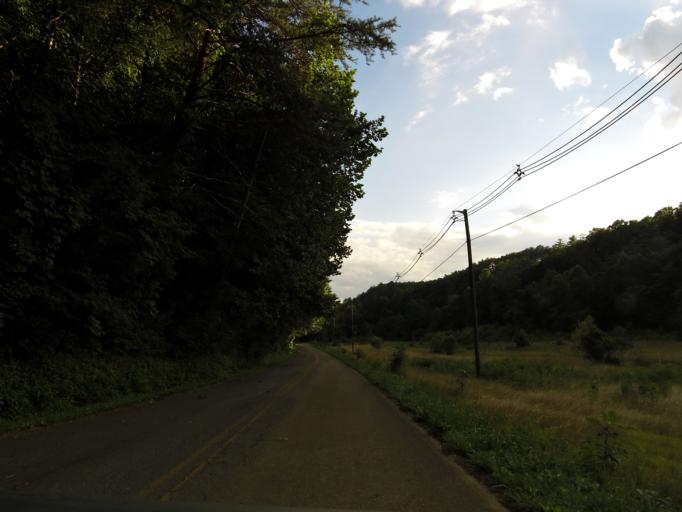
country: US
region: Tennessee
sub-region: Blount County
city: Maryville
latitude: 35.5664
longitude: -84.0020
